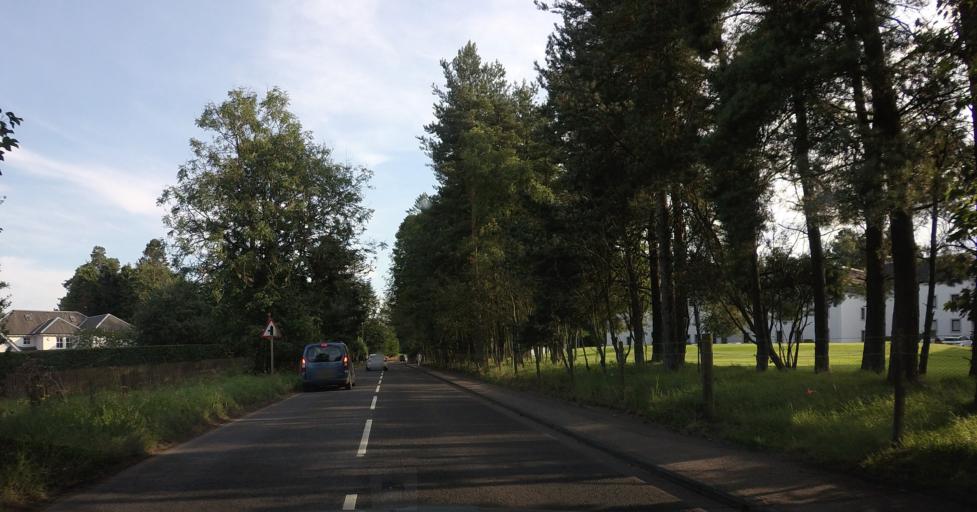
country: GB
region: Scotland
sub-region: Perth and Kinross
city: Auchterarder
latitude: 56.2849
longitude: -3.7452
